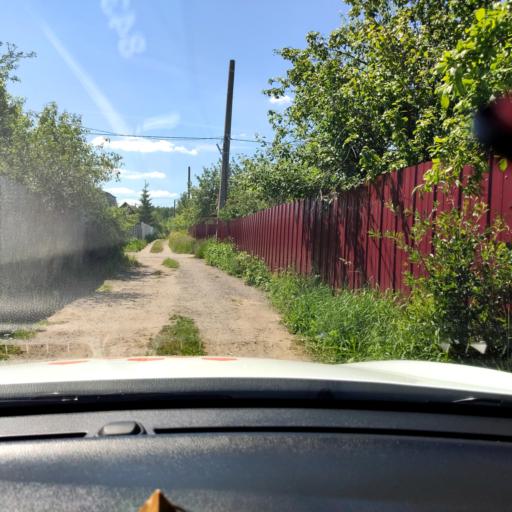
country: RU
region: Tatarstan
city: Vysokaya Gora
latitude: 55.8114
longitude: 49.2849
